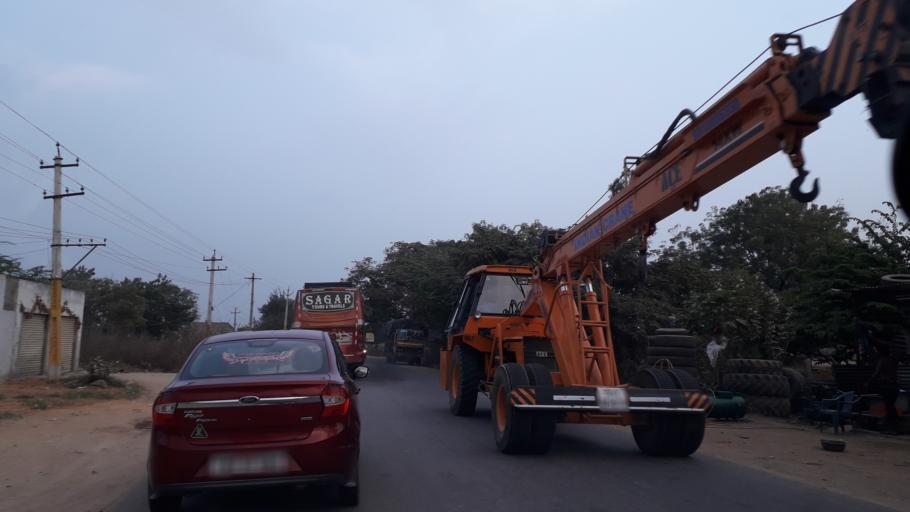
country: IN
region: Telangana
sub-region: Medak
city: Patancheru
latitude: 17.5118
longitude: 78.2217
